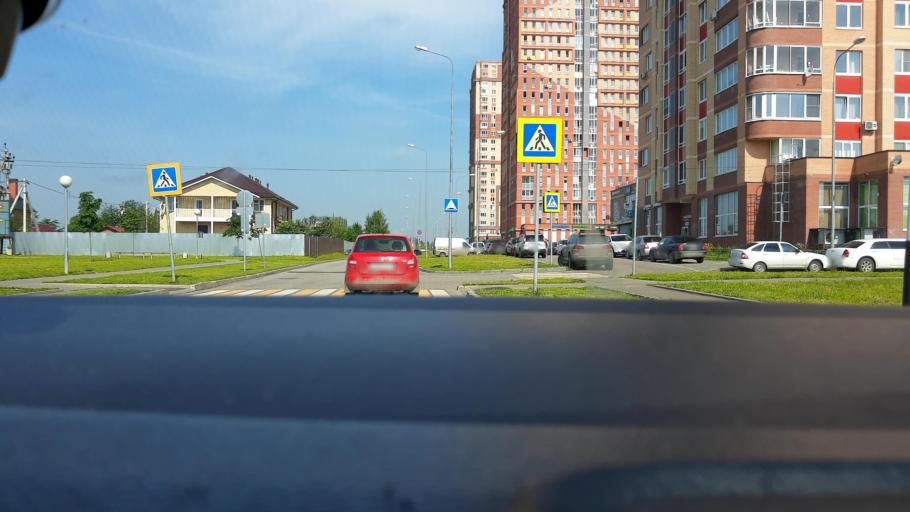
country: RU
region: Moskovskaya
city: Shcherbinka
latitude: 55.5021
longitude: 37.5387
